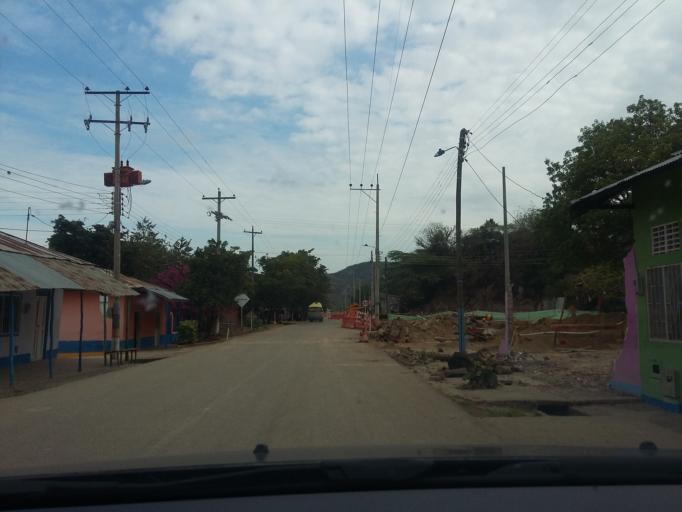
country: CO
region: Cundinamarca
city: Guataqui
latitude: 4.5151
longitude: -74.7891
